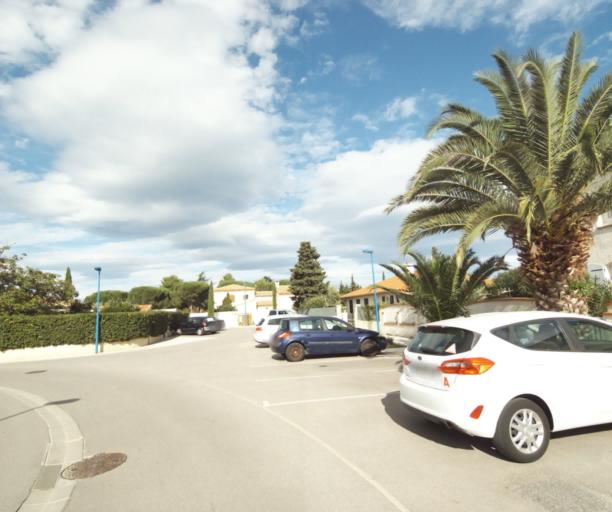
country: FR
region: Languedoc-Roussillon
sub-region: Departement des Pyrenees-Orientales
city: Argelers
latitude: 42.5464
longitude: 3.0123
